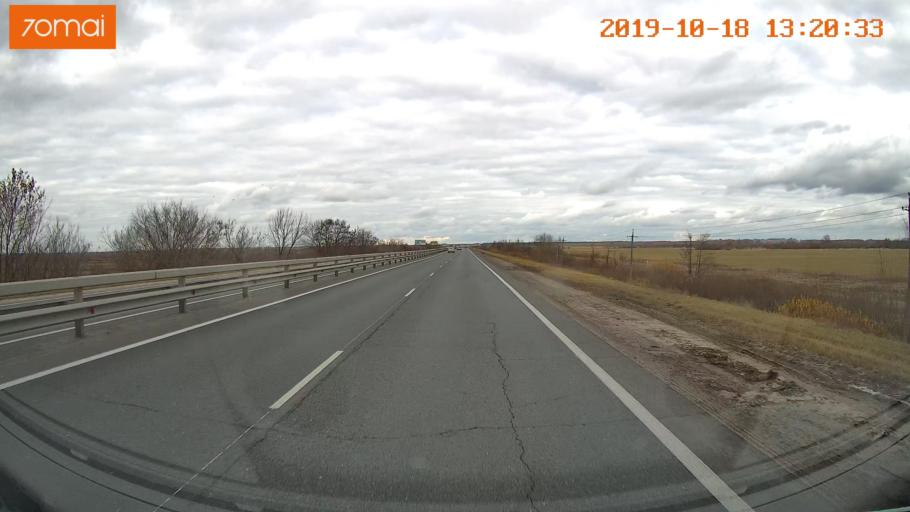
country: RU
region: Rjazan
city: Polyany
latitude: 54.6823
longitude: 39.8327
